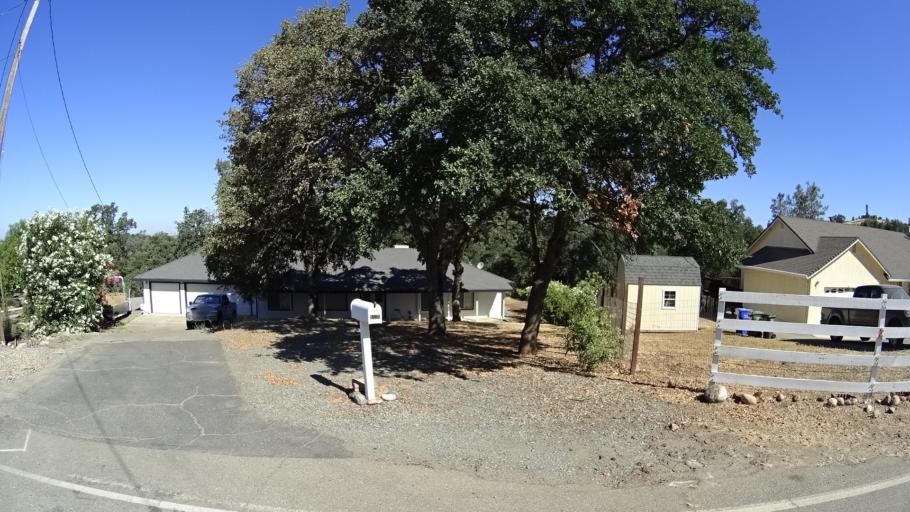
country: US
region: California
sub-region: Calaveras County
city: Rancho Calaveras
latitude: 38.0961
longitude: -120.8580
